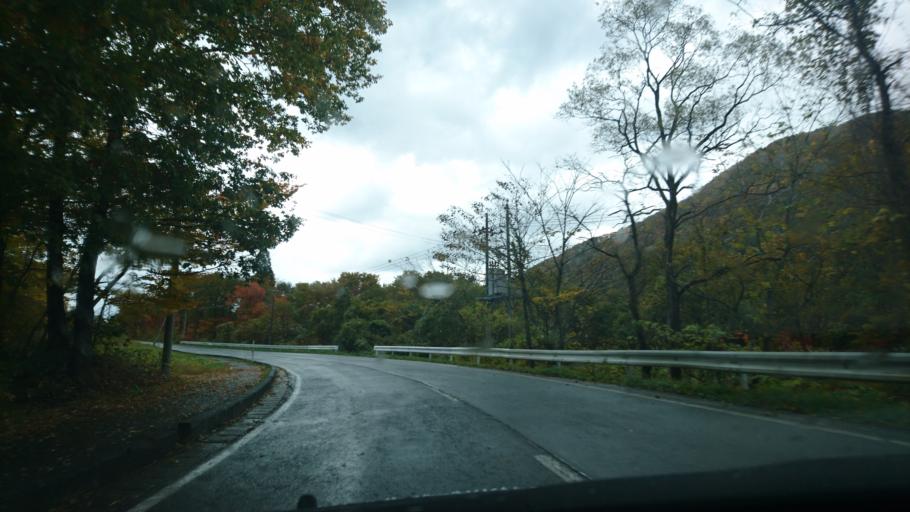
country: JP
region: Iwate
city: Shizukuishi
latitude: 39.6121
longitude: 140.9437
